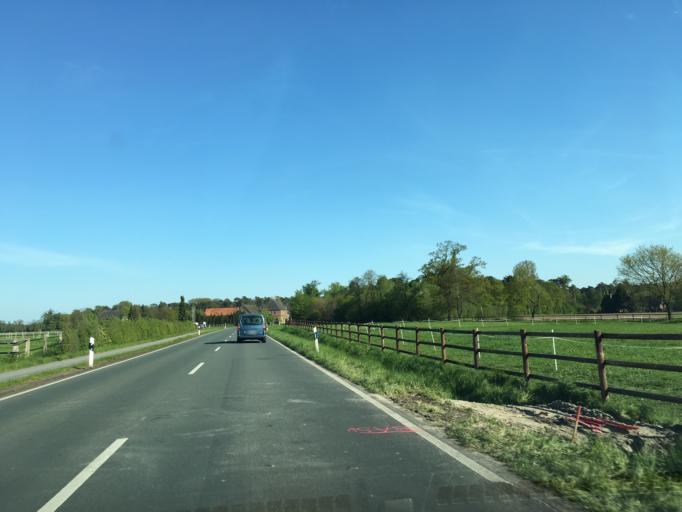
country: DE
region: North Rhine-Westphalia
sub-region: Regierungsbezirk Munster
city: Senden
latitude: 51.8501
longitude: 7.5049
